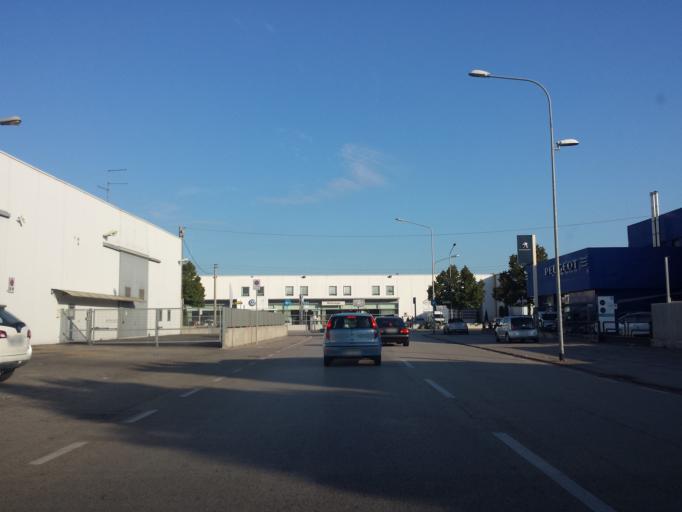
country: IT
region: Veneto
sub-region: Provincia di Vicenza
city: Creazzo
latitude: 45.5269
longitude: 11.5019
